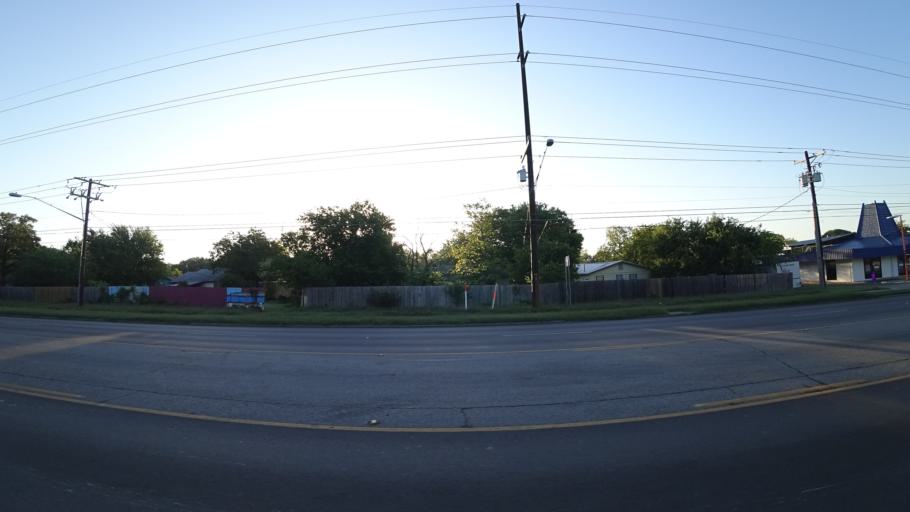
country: US
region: Texas
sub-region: Travis County
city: Wells Branch
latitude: 30.3589
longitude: -97.6994
